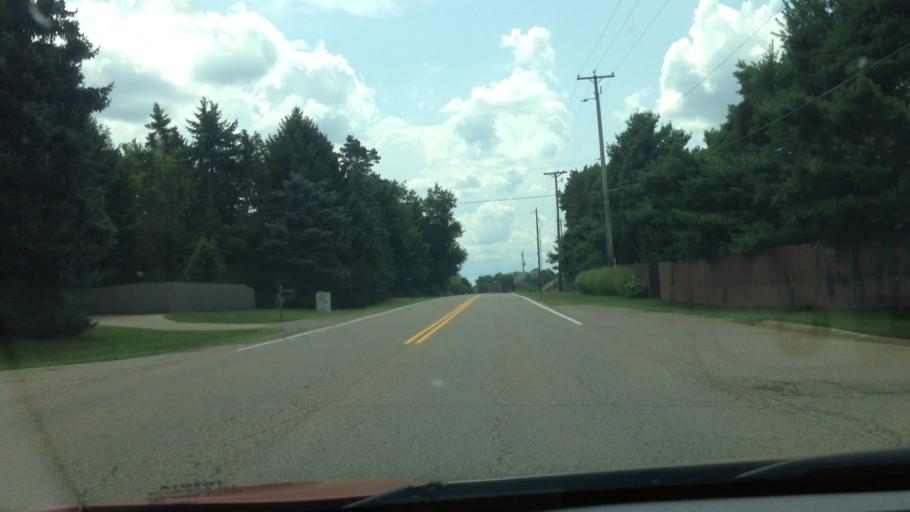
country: US
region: Ohio
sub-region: Stark County
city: Perry Heights
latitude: 40.8285
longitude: -81.4632
